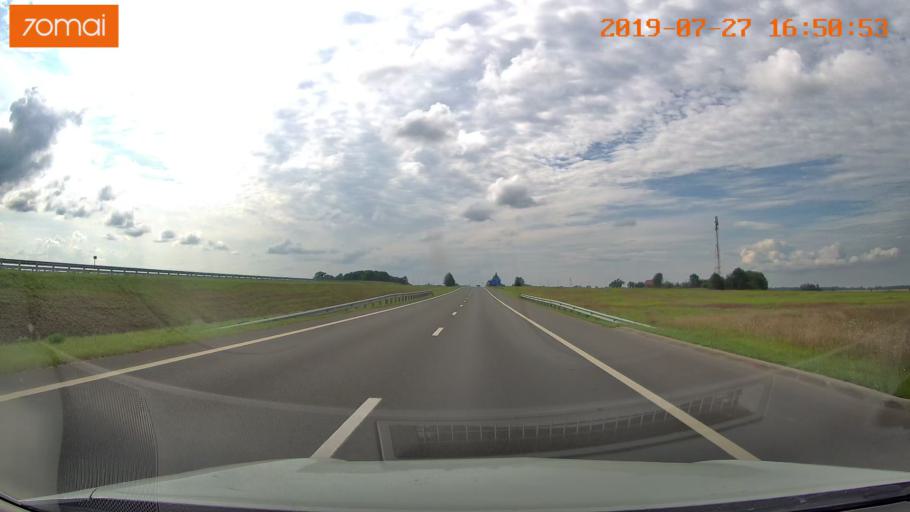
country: RU
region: Kaliningrad
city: Gvardeysk
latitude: 54.6798
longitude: 20.9017
